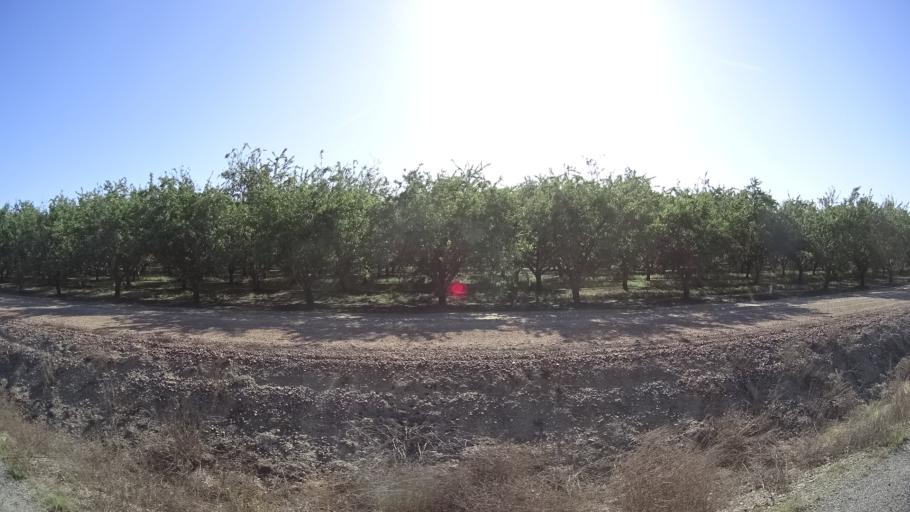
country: US
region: California
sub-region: Glenn County
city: Hamilton City
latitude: 39.7065
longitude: -122.0548
